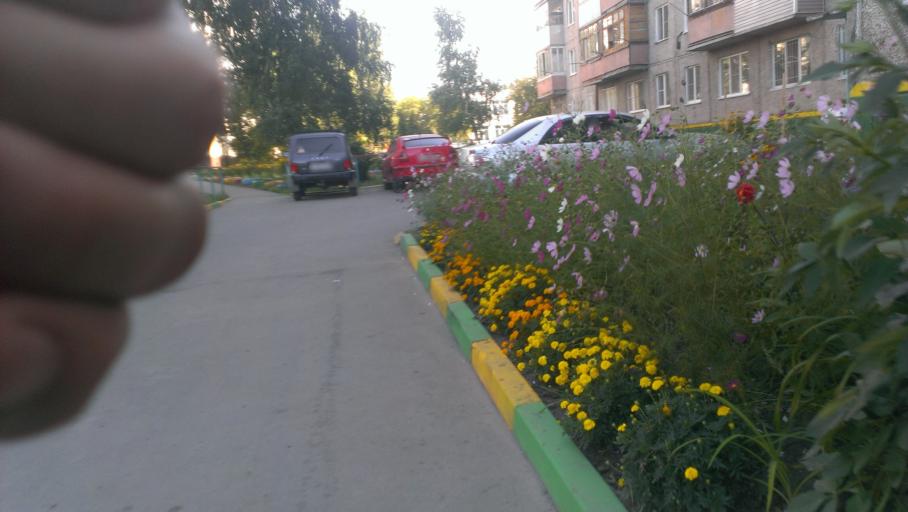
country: RU
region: Altai Krai
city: Novosilikatnyy
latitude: 53.3062
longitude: 83.6225
